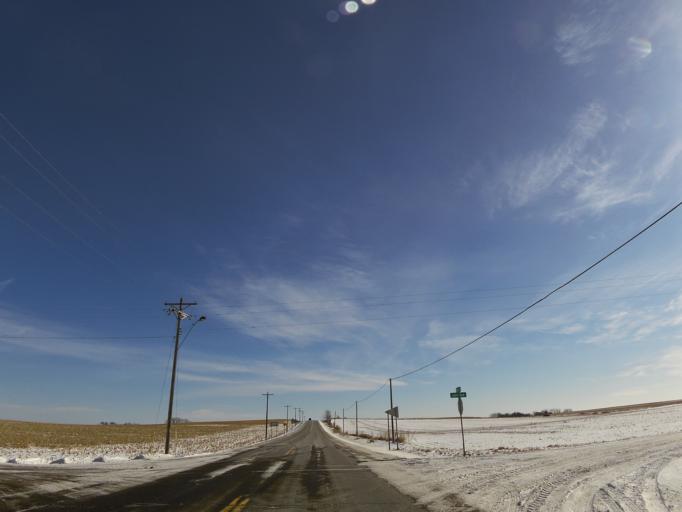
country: US
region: Minnesota
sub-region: Dakota County
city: Hastings
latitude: 44.7568
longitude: -92.9241
